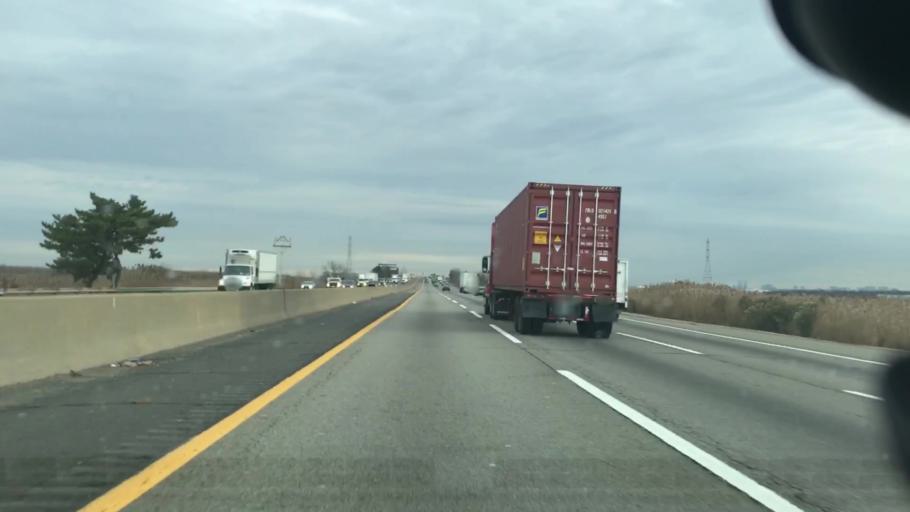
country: US
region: New Jersey
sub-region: Bergen County
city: North Arlington
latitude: 40.7769
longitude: -74.1006
